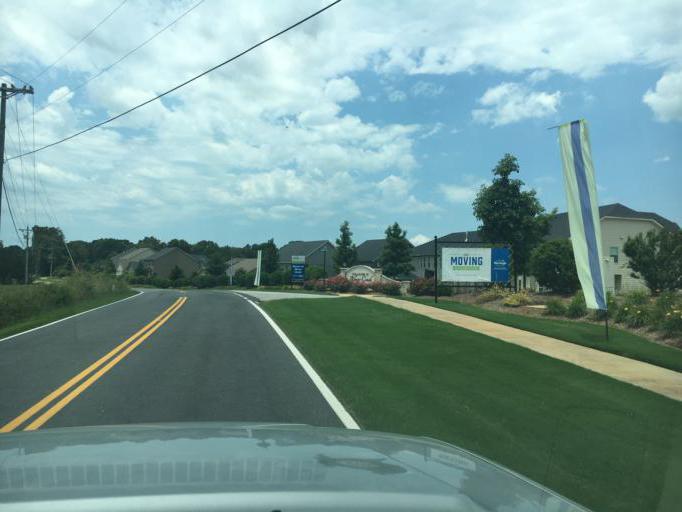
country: US
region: South Carolina
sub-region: Spartanburg County
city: Duncan
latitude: 34.8749
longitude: -82.1710
